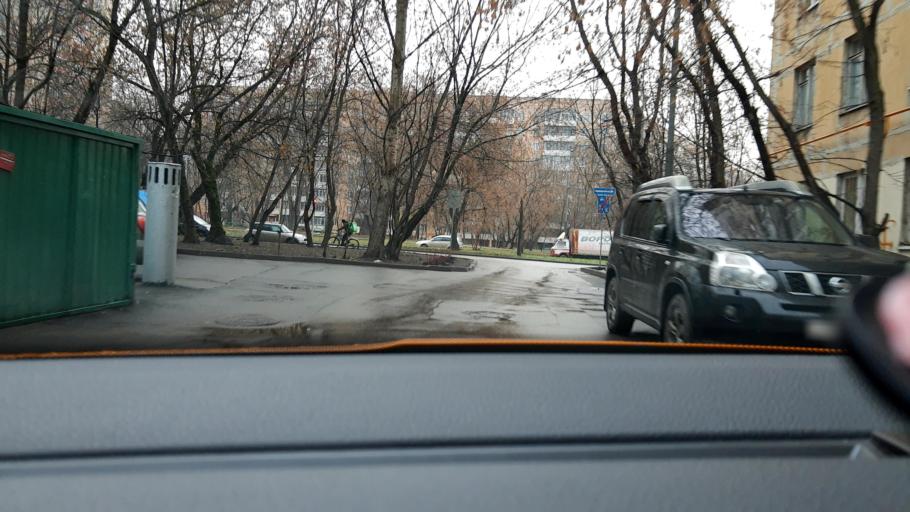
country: RU
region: Moscow
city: Rostokino
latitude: 55.8206
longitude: 37.6557
